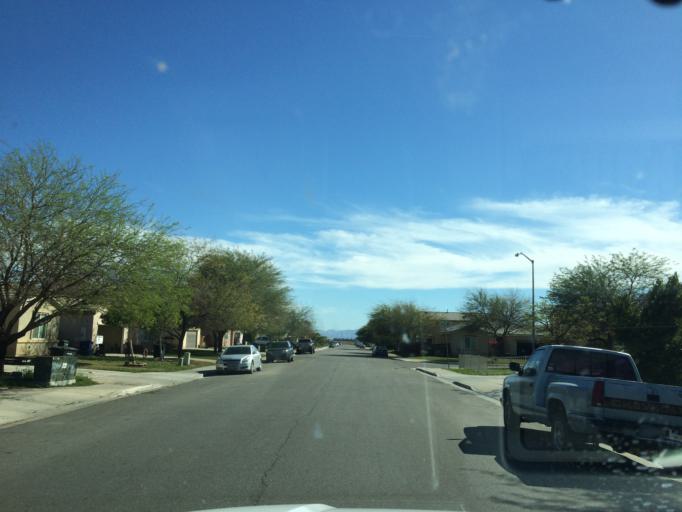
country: US
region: California
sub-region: Imperial County
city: Heber
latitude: 32.7375
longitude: -115.5364
